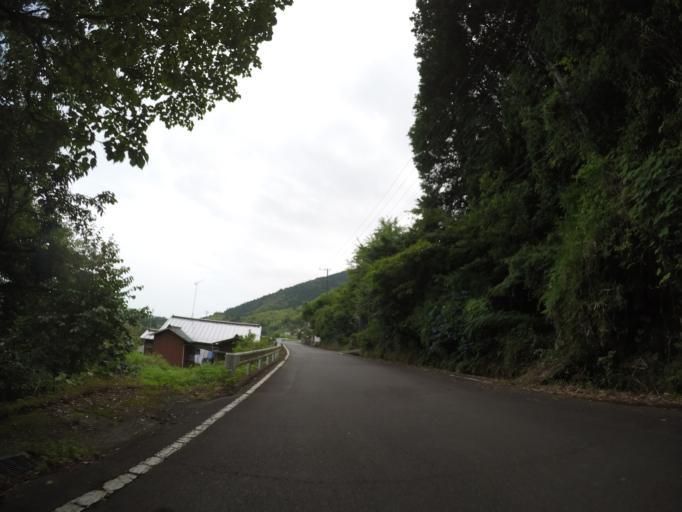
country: JP
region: Shizuoka
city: Fujinomiya
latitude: 35.2426
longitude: 138.5555
